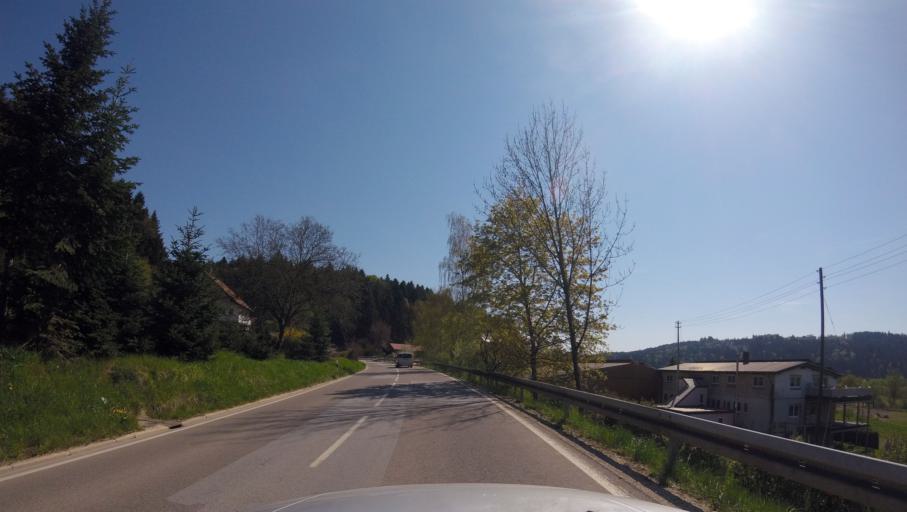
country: DE
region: Baden-Wuerttemberg
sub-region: Regierungsbezirk Stuttgart
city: Lorch
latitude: 48.7914
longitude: 9.7358
